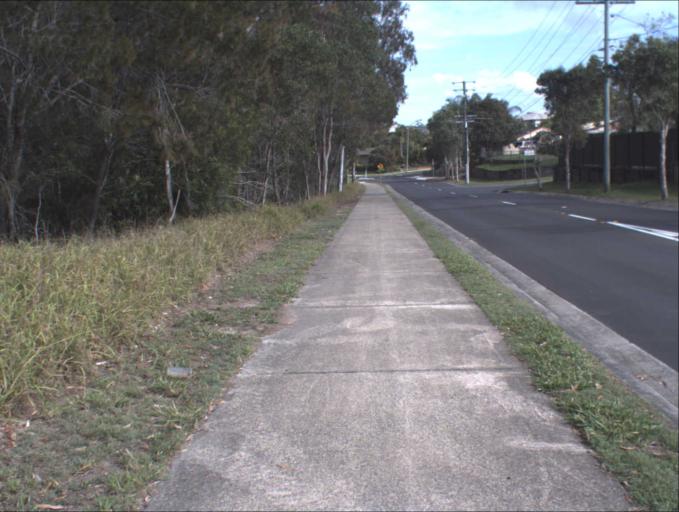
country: AU
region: Queensland
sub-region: Logan
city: Woodridge
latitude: -27.6671
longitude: 153.0635
